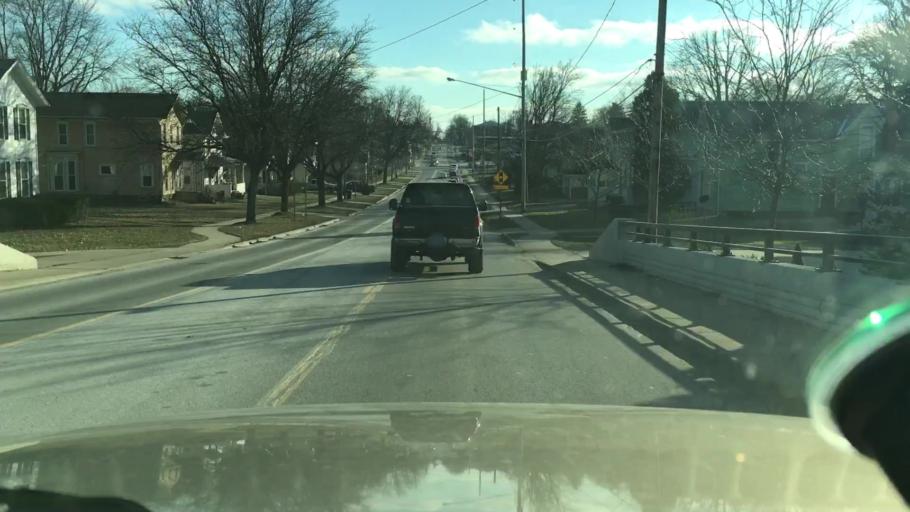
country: US
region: Michigan
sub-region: Jackson County
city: Jackson
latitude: 42.2528
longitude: -84.4235
